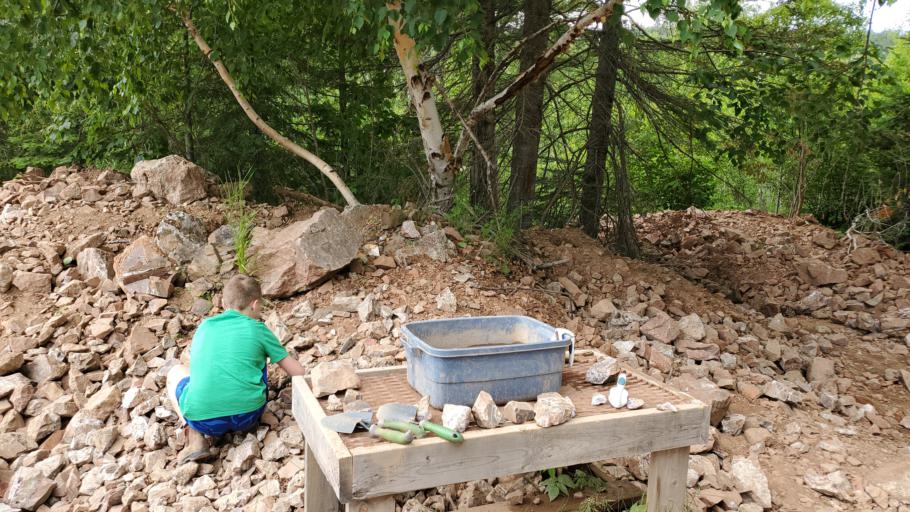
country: CA
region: Ontario
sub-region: Thunder Bay District
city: Thunder Bay
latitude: 48.6865
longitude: -88.6658
